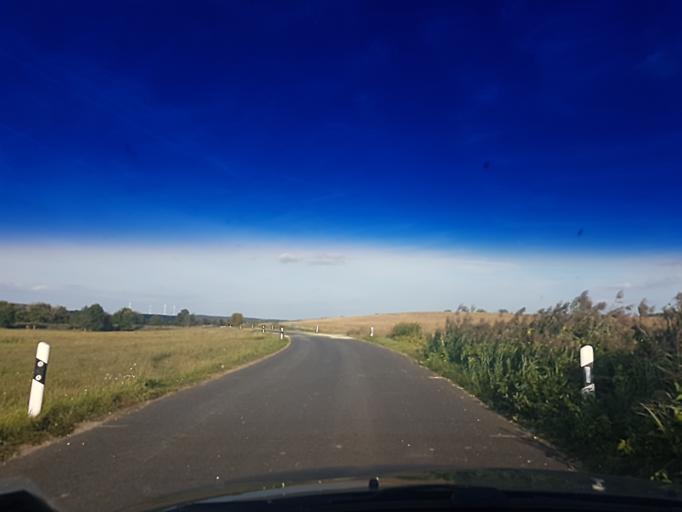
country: DE
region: Bavaria
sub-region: Regierungsbezirk Mittelfranken
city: Wachenroth
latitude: 49.7422
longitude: 10.6770
